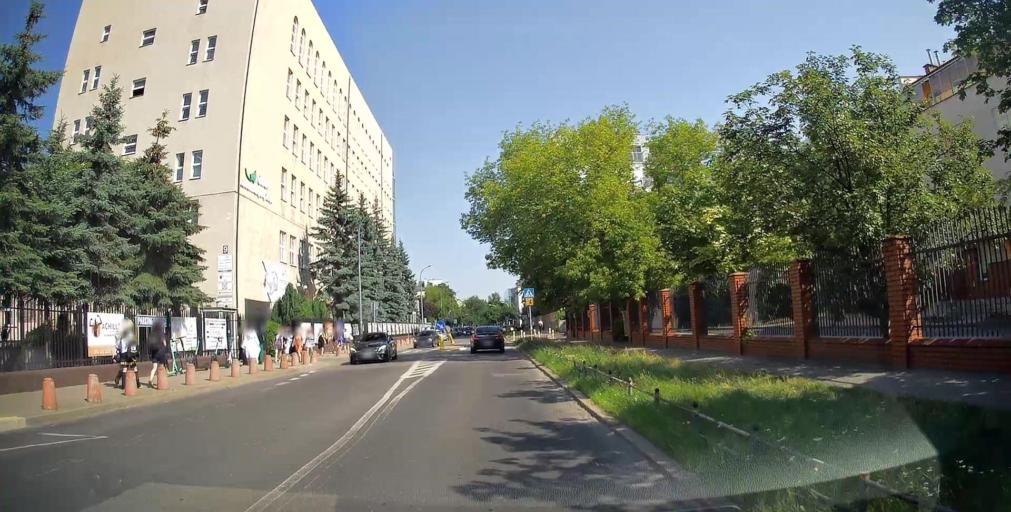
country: PL
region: Masovian Voivodeship
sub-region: Warszawa
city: Mokotow
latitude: 52.2004
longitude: 21.0462
